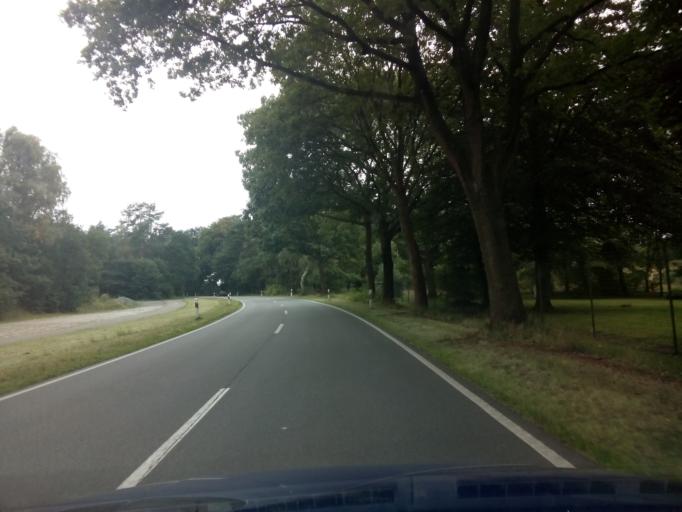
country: DE
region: Lower Saxony
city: Kohlen
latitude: 53.5184
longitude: 8.8665
